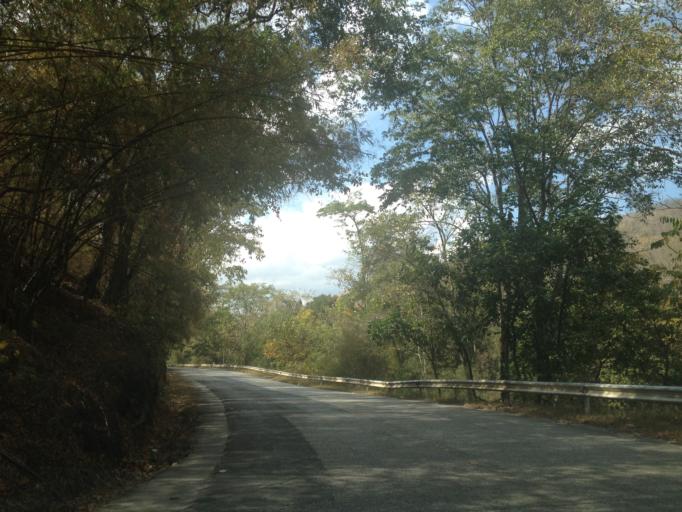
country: TH
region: Chiang Mai
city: Hot
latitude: 18.2331
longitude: 98.5273
